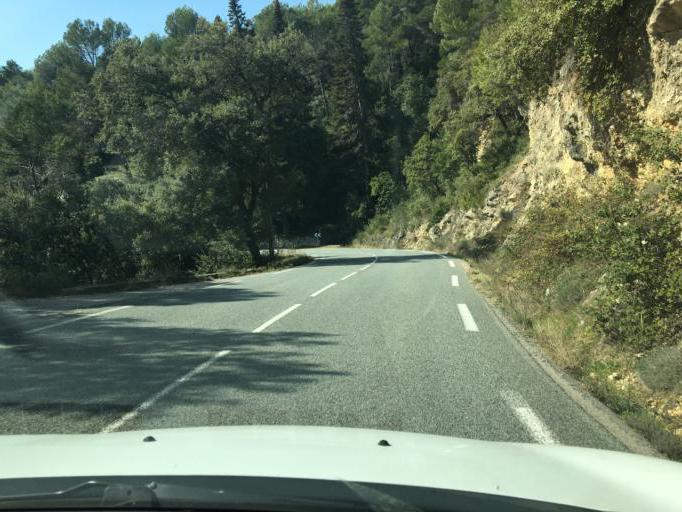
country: FR
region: Provence-Alpes-Cote d'Azur
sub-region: Departement du Var
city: Callas
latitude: 43.5991
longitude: 6.5472
